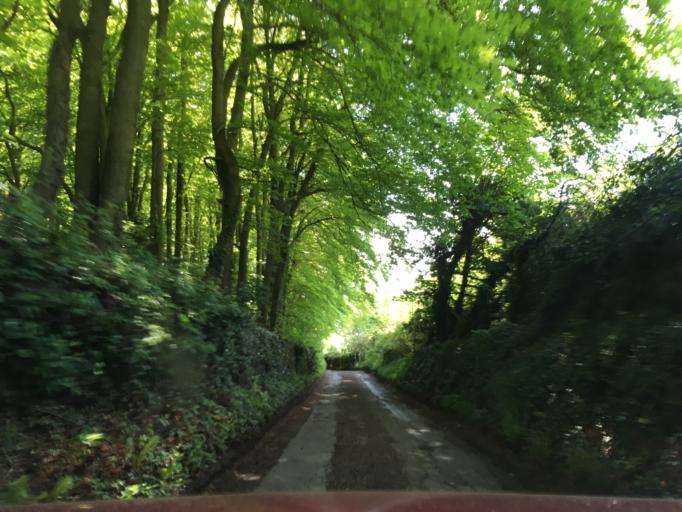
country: GB
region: England
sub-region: Gloucestershire
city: Brimscombe
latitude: 51.7253
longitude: -2.1854
